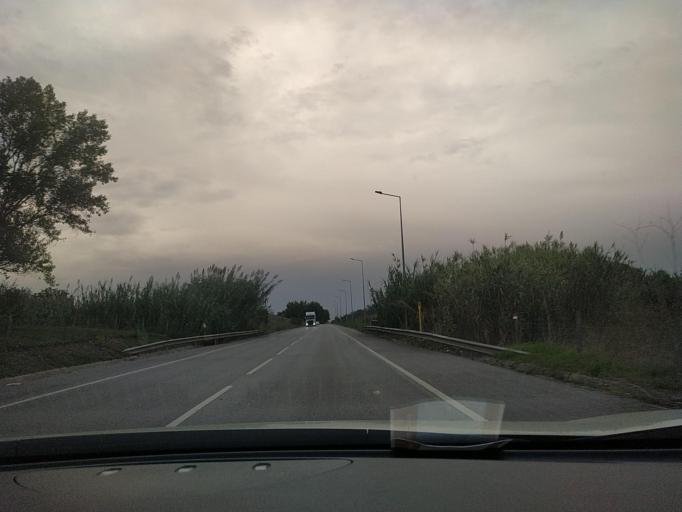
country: PT
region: Lisbon
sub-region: Loures
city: Santa Iria da Azoia
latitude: 38.8678
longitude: -9.0917
